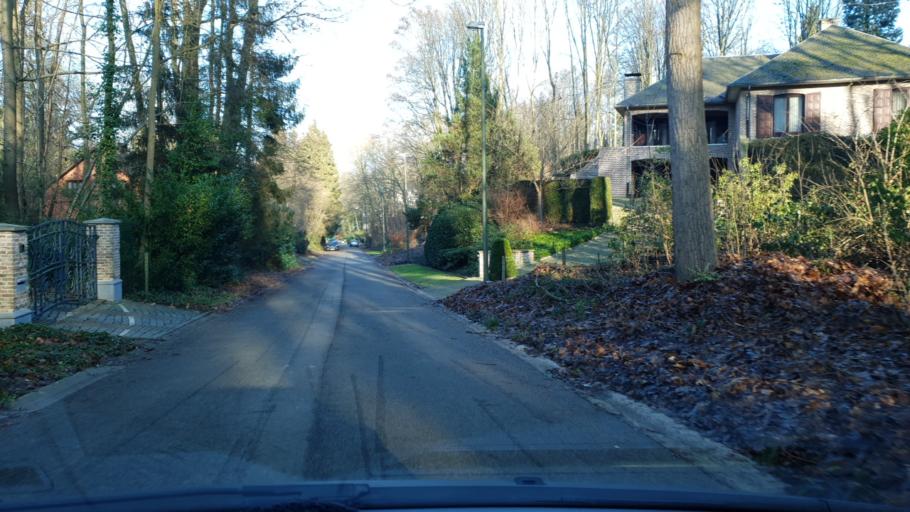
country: BE
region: Flanders
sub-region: Provincie Vlaams-Brabant
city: Bertem
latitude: 50.8857
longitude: 4.6403
